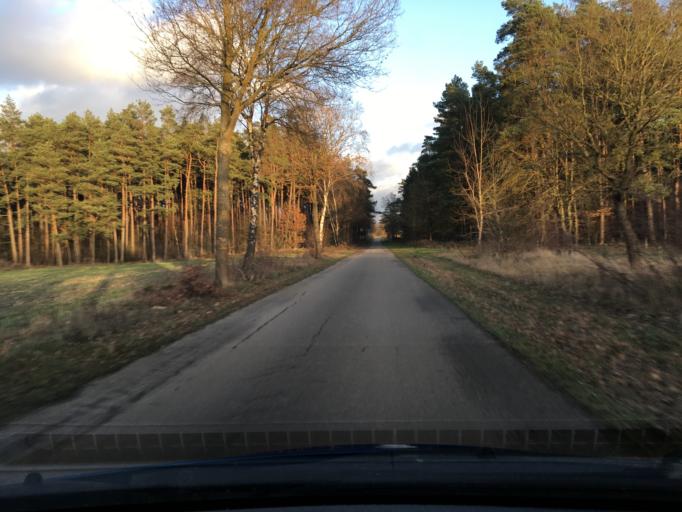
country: DE
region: Lower Saxony
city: Soderstorf
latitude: 53.1110
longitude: 10.1515
